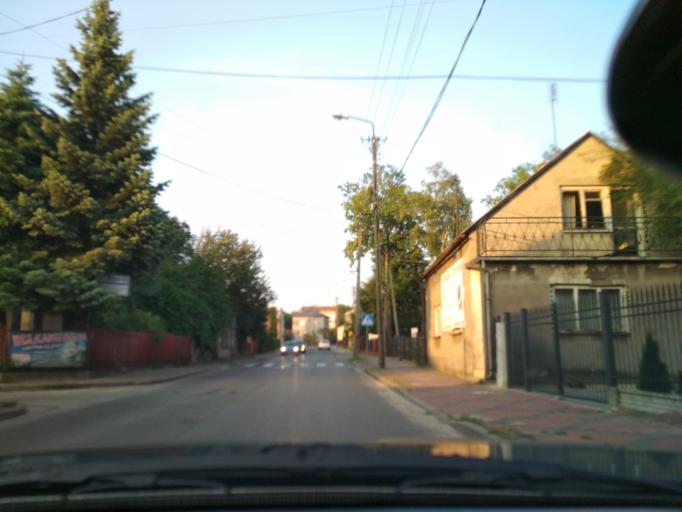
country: PL
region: Lesser Poland Voivodeship
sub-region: Powiat olkuski
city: Wolbrom
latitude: 50.3888
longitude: 19.7593
